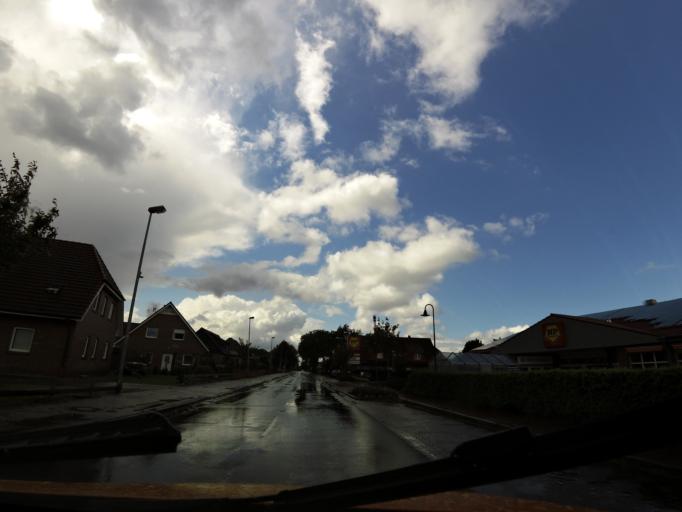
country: DE
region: Lower Saxony
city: Hatten
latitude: 53.1203
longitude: 8.3333
